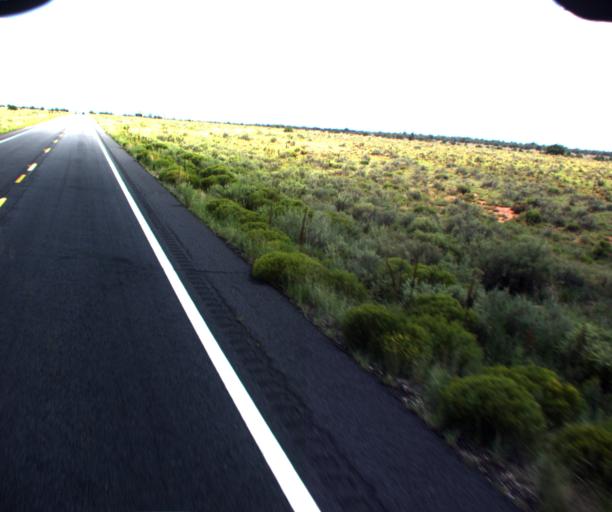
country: US
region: Arizona
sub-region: Coconino County
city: Grand Canyon Village
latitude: 35.6835
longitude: -112.1352
